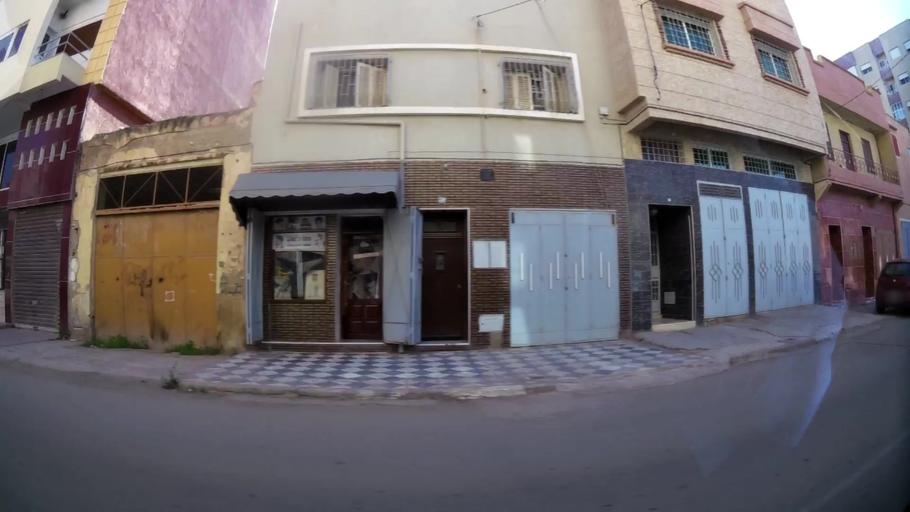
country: MA
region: Oriental
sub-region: Oujda-Angad
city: Oujda
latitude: 34.6881
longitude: -1.9183
